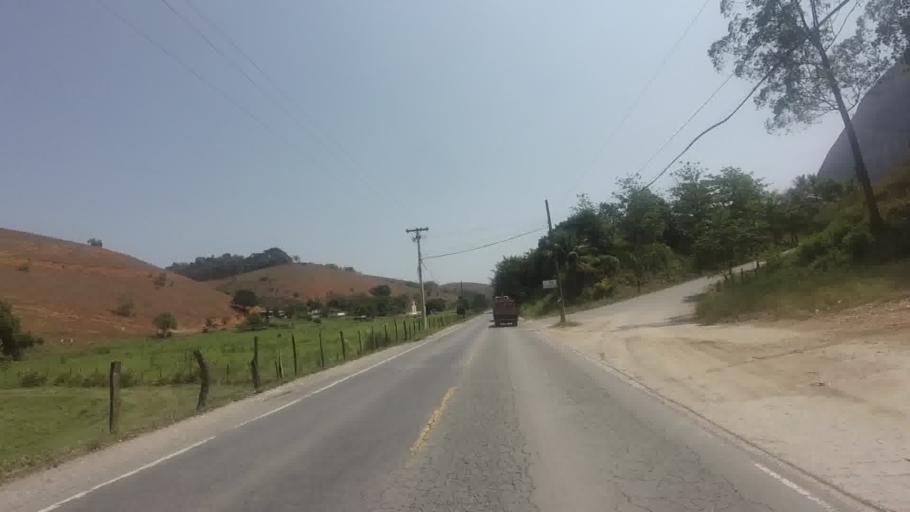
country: BR
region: Espirito Santo
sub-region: Rio Novo Do Sul
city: Rio Novo do Sul
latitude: -20.8850
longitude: -41.0054
